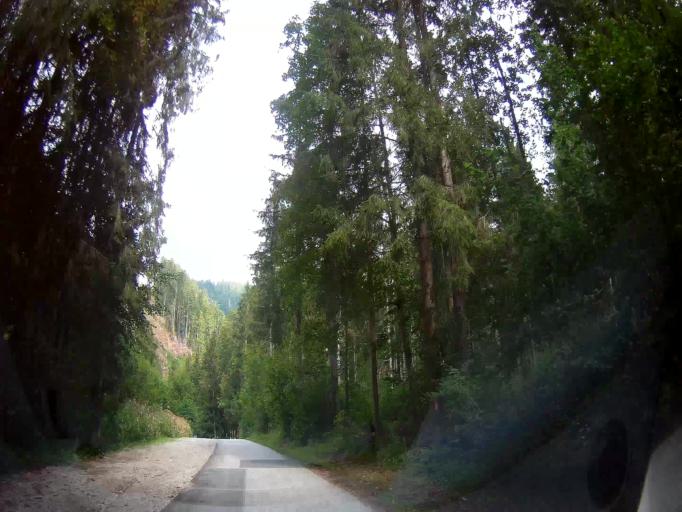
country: AT
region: Salzburg
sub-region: Politischer Bezirk Zell am See
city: Leogang
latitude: 47.4523
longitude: 12.7568
